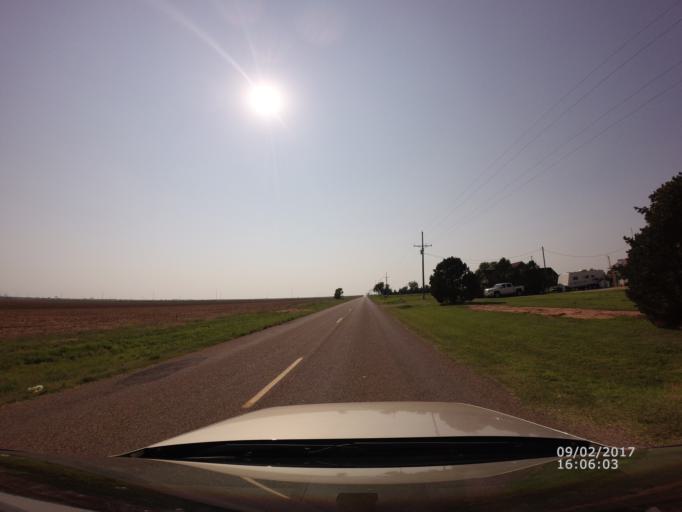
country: US
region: New Mexico
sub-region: Curry County
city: Clovis
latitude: 34.4484
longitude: -103.2090
